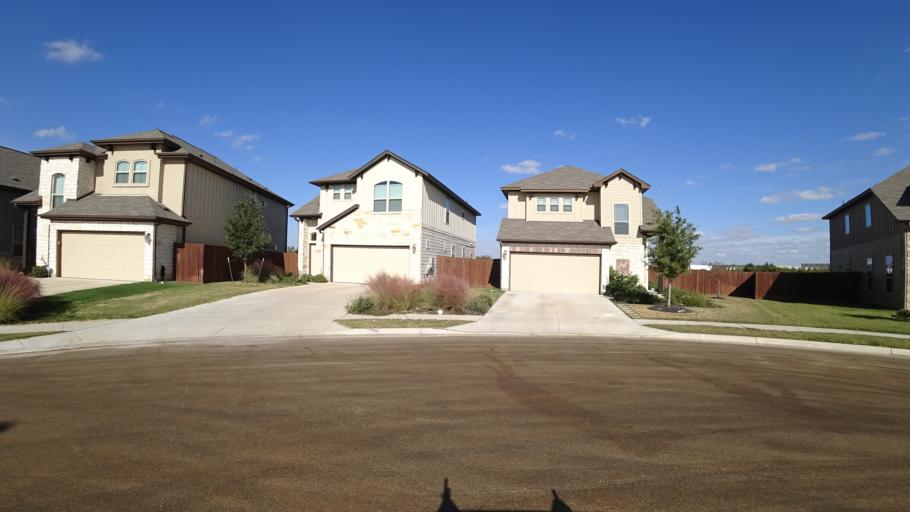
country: US
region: Texas
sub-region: Travis County
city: Wells Branch
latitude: 30.4695
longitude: -97.6803
